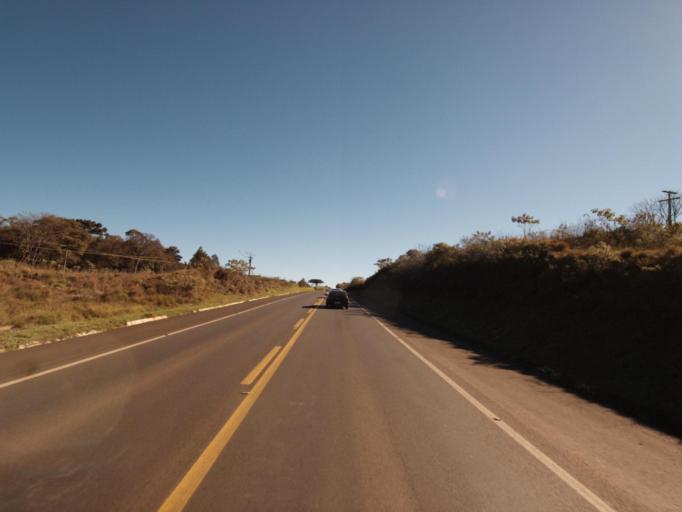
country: BR
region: Santa Catarina
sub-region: Xanxere
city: Xanxere
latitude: -26.9149
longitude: -52.4815
